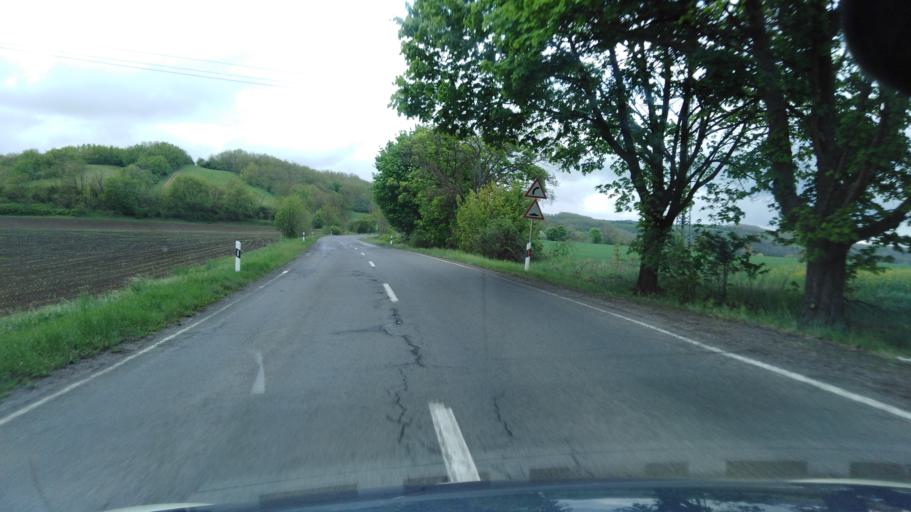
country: HU
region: Nograd
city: Szecseny
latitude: 48.1171
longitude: 19.5495
